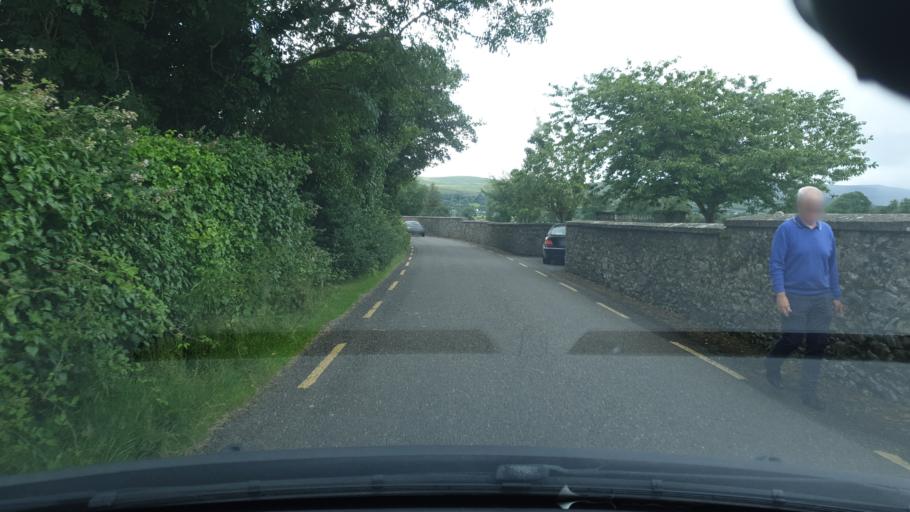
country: IE
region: Munster
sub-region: Ciarrai
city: Tralee
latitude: 52.2526
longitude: -9.6445
